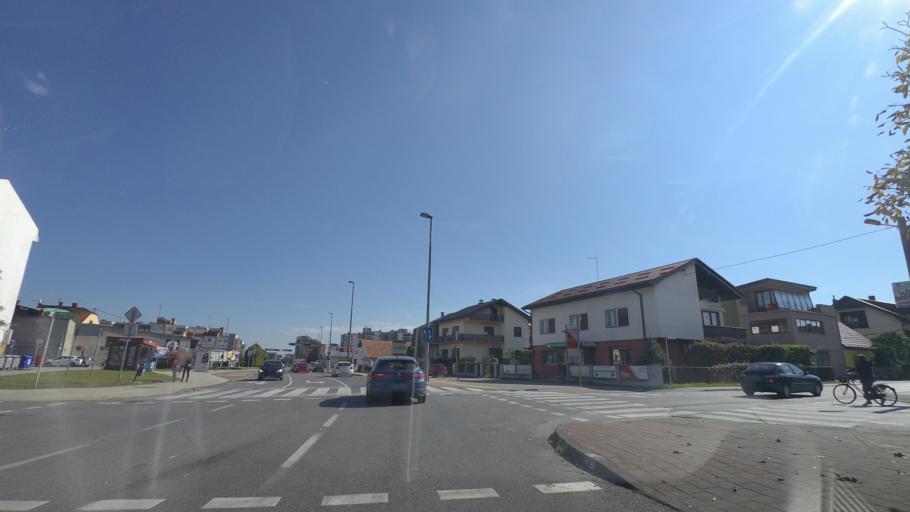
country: HR
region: Karlovacka
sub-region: Grad Karlovac
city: Karlovac
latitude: 45.4833
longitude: 15.5456
